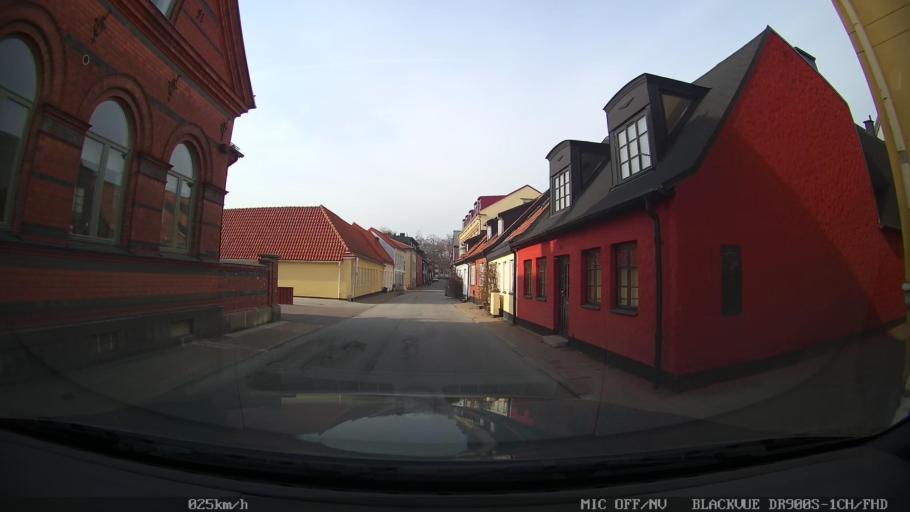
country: SE
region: Skane
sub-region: Ystads Kommun
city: Ystad
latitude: 55.4300
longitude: 13.8174
